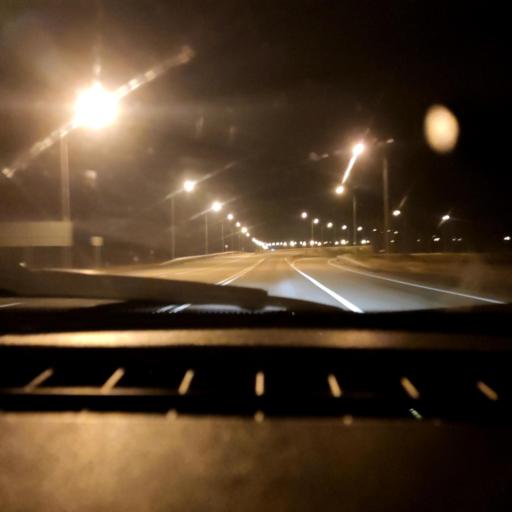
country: RU
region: Bashkortostan
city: Kushnarenkovo
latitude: 55.0627
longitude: 55.4233
